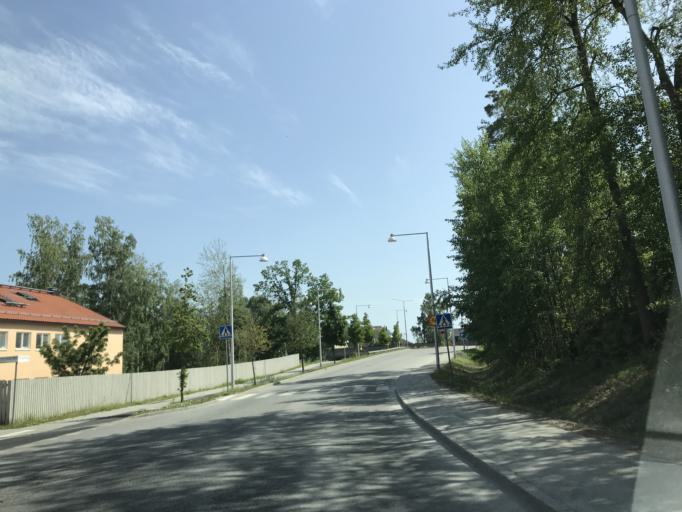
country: SE
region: Stockholm
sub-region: Solna Kommun
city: Rasunda
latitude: 59.3804
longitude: 17.9899
